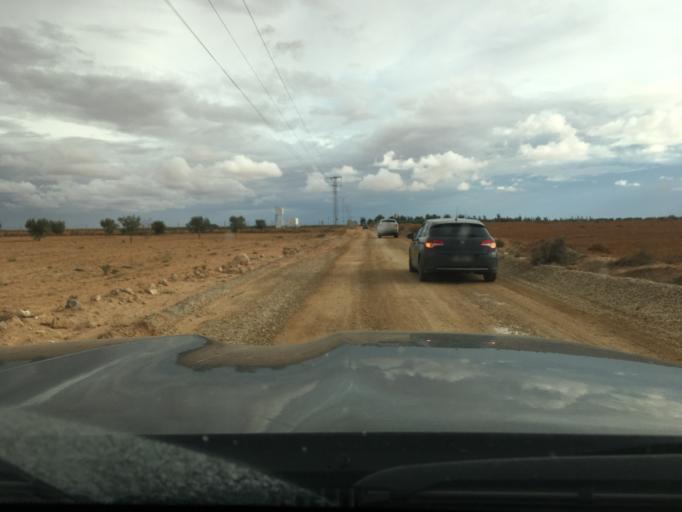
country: TN
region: Madanin
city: Medenine
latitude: 33.2781
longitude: 10.5584
